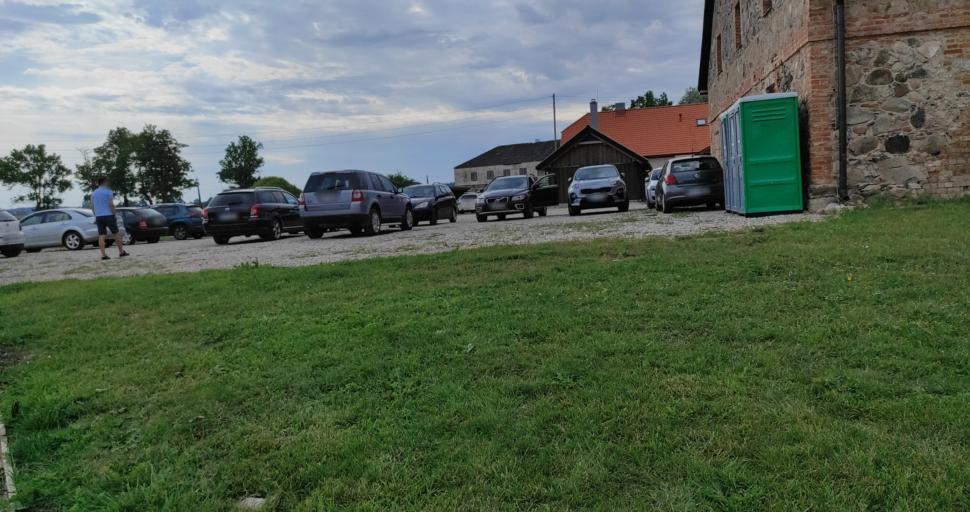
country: LV
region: Talsu Rajons
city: Talsi
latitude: 57.2258
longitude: 22.7642
